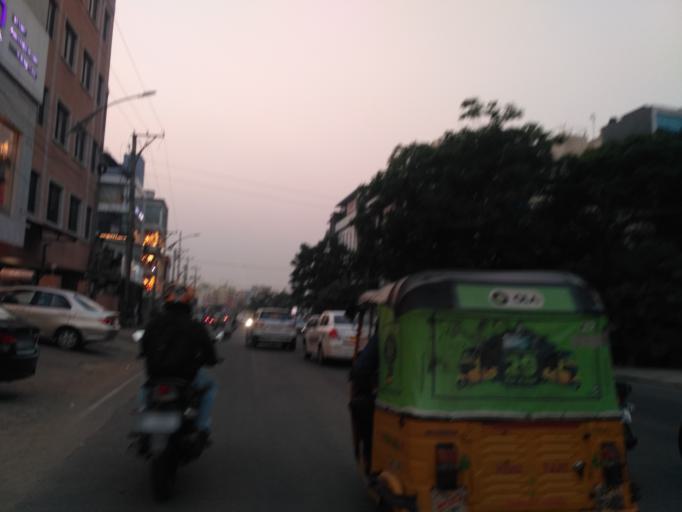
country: IN
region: Telangana
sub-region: Rangareddi
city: Kukatpalli
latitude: 17.4418
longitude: 78.3969
